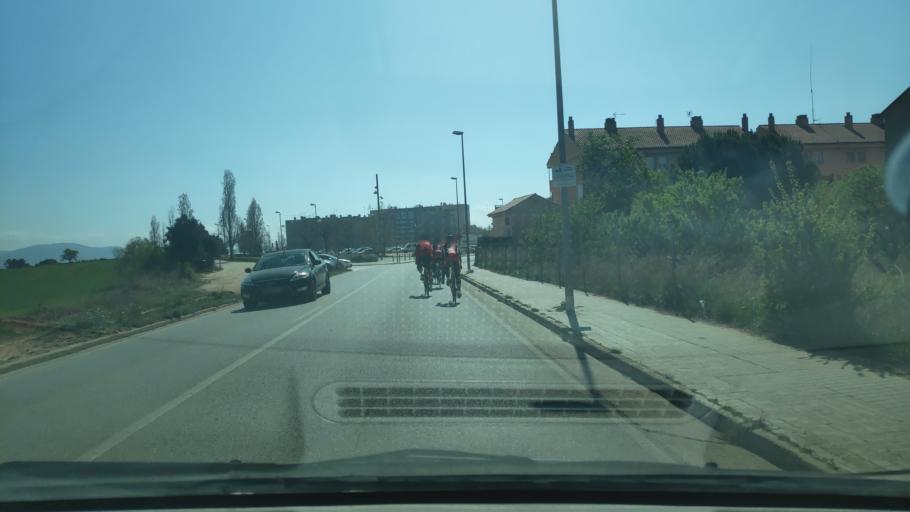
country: ES
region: Catalonia
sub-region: Provincia de Barcelona
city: Sabadell
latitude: 41.5529
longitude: 2.1268
